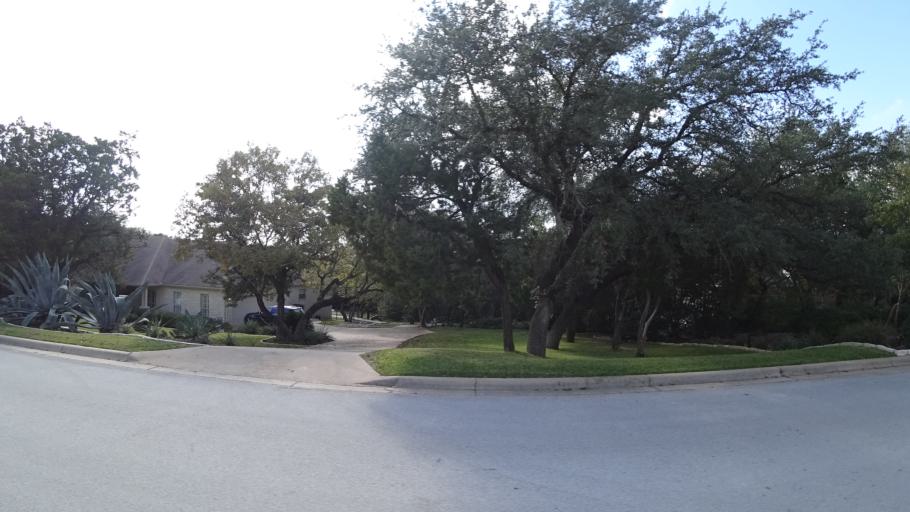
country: US
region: Texas
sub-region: Travis County
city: Barton Creek
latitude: 30.3142
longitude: -97.8720
